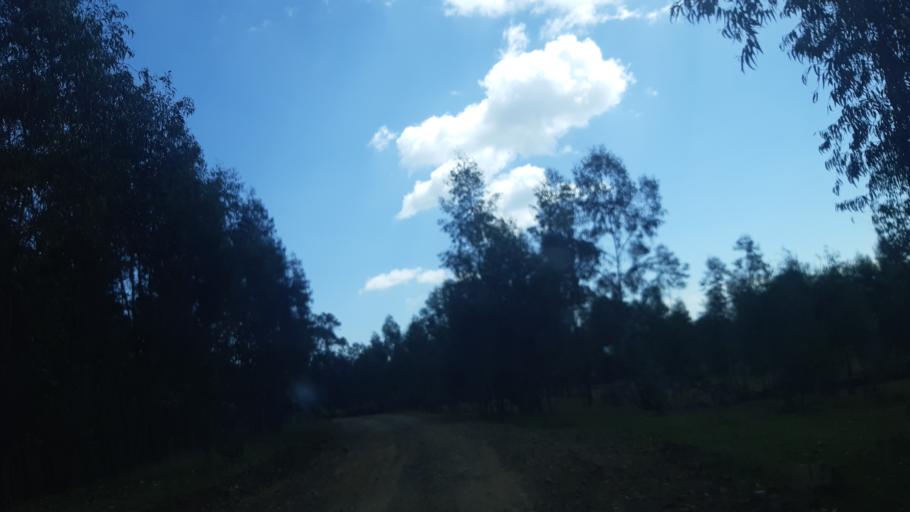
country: ET
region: Amhara
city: Dabat
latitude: 13.3562
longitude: 37.3865
